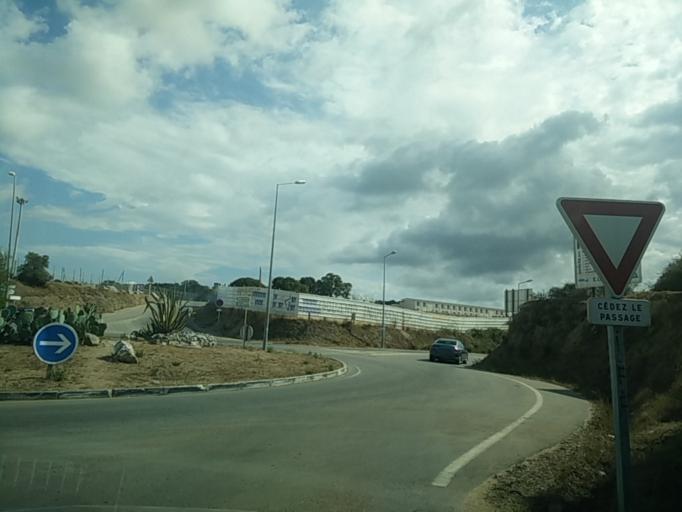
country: FR
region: Corsica
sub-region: Departement de la Corse-du-Sud
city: Ajaccio
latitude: 41.9465
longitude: 8.7721
